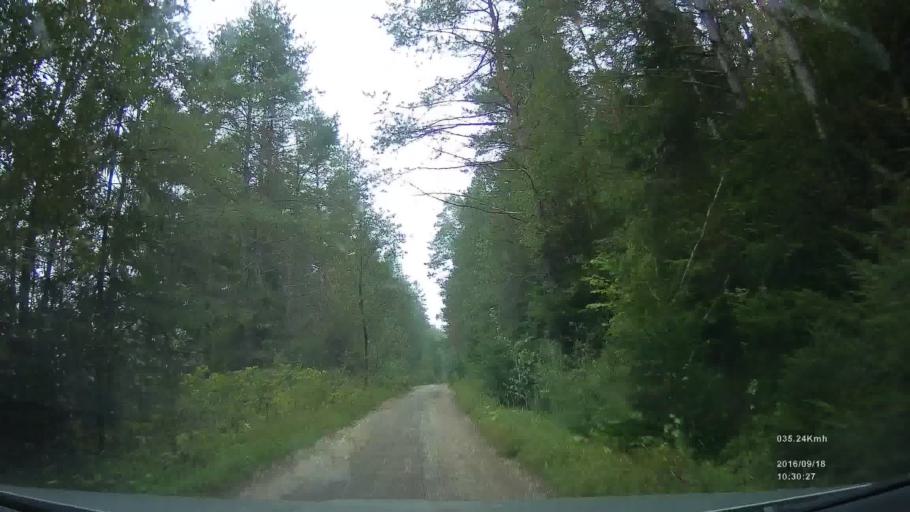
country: SK
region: Kosicky
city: Spisska Nova Ves
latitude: 48.9580
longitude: 20.6237
